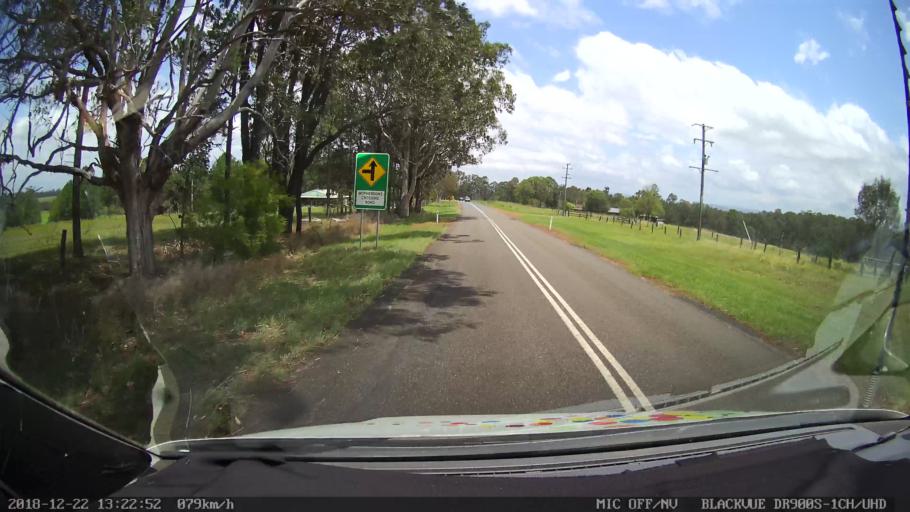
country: AU
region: New South Wales
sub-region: Clarence Valley
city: Coutts Crossing
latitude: -29.7917
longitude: 152.9100
